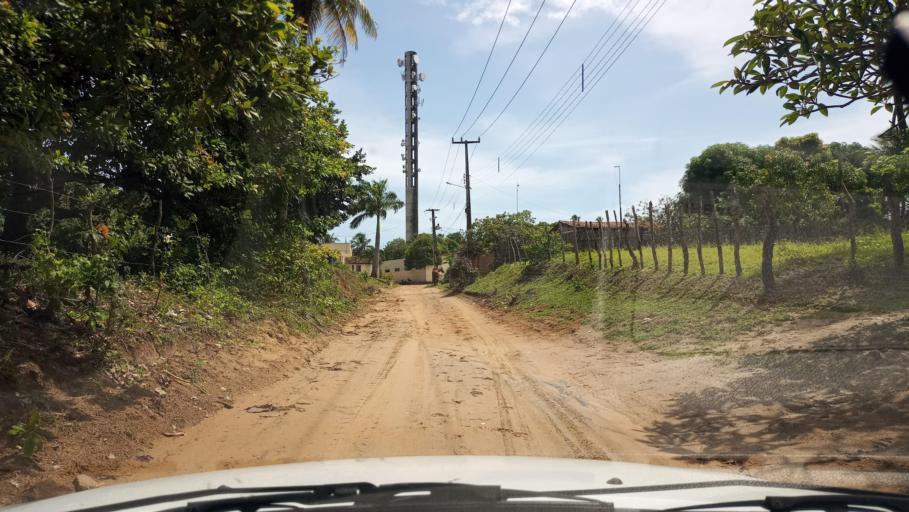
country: BR
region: Rio Grande do Norte
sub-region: Maxaranguape
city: Sao Miguel
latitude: -5.4623
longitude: -35.2935
